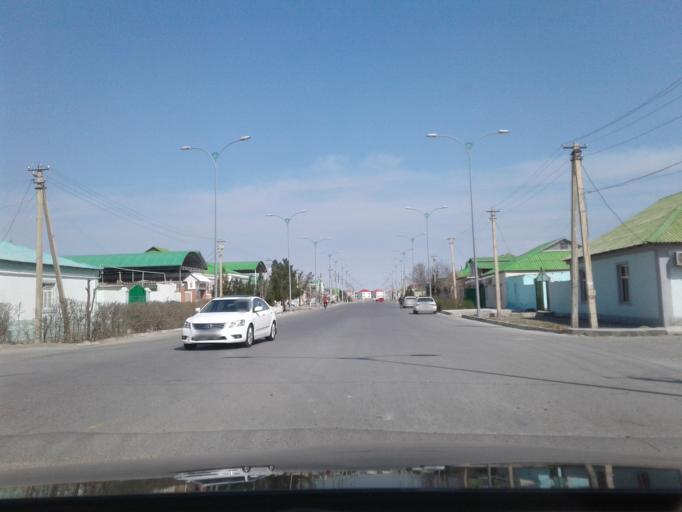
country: TM
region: Ahal
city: Ashgabat
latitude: 37.9870
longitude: 58.4005
